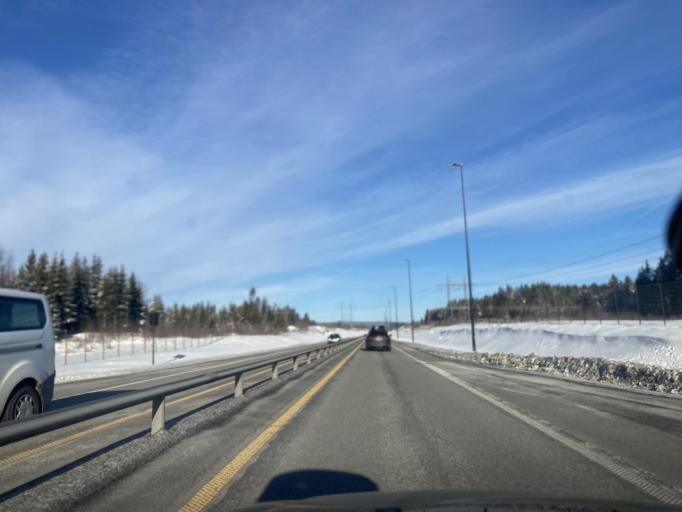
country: NO
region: Hedmark
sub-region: Loten
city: Loten
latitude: 60.8039
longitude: 11.2898
